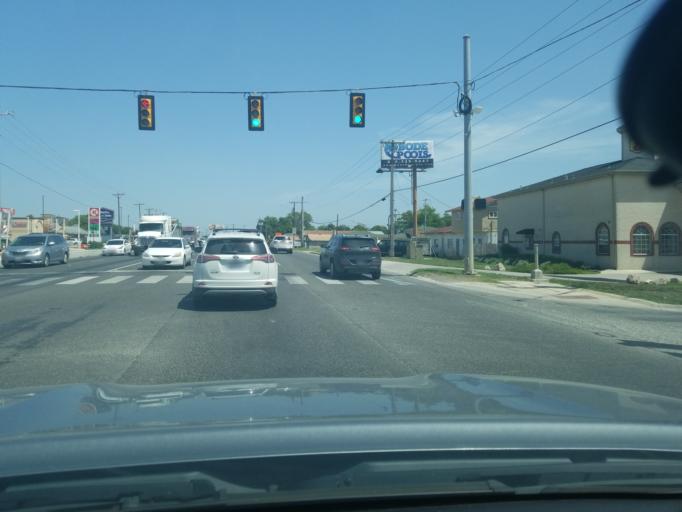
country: US
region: Texas
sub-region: Guadalupe County
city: Lake Dunlap
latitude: 29.6985
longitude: -98.0916
